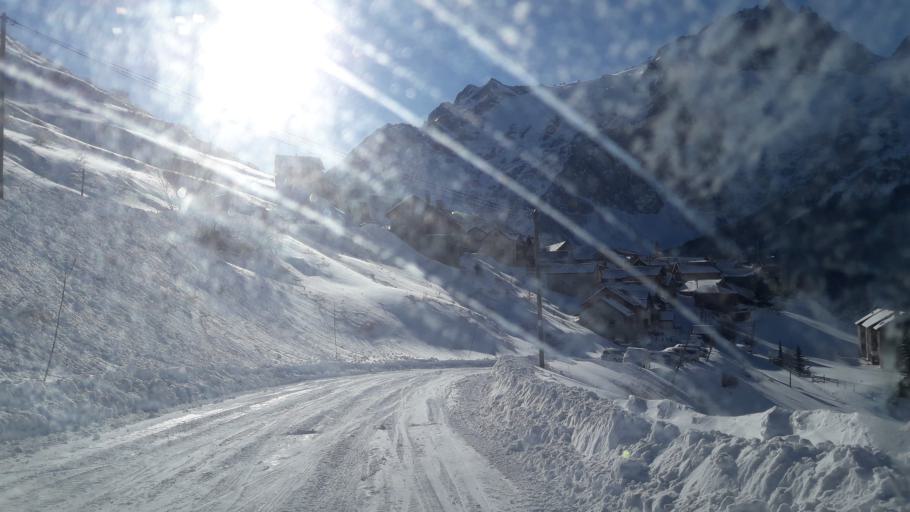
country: FR
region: Rhone-Alpes
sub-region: Departement de l'Isere
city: Mont-de-Lans
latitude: 45.0564
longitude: 6.2829
